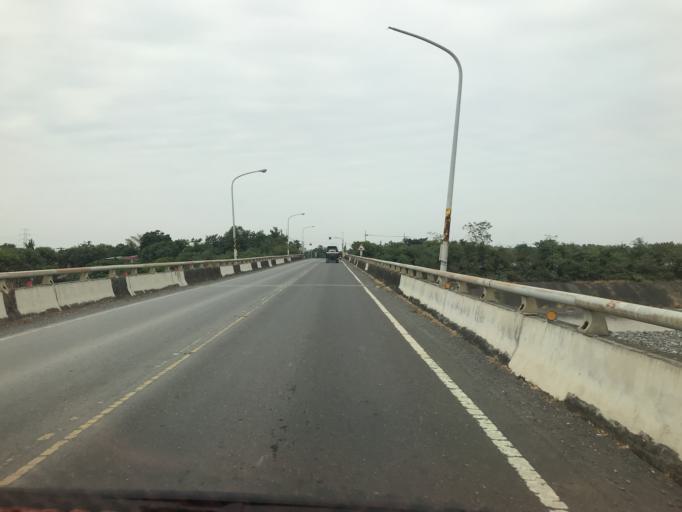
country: TW
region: Taiwan
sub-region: Pingtung
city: Pingtung
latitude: 22.4932
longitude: 120.5933
